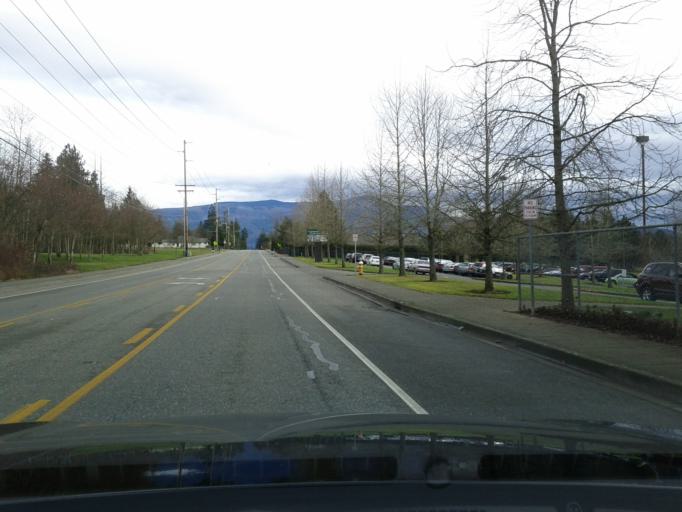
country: US
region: Washington
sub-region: Skagit County
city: Mount Vernon
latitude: 48.4428
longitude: -122.3012
